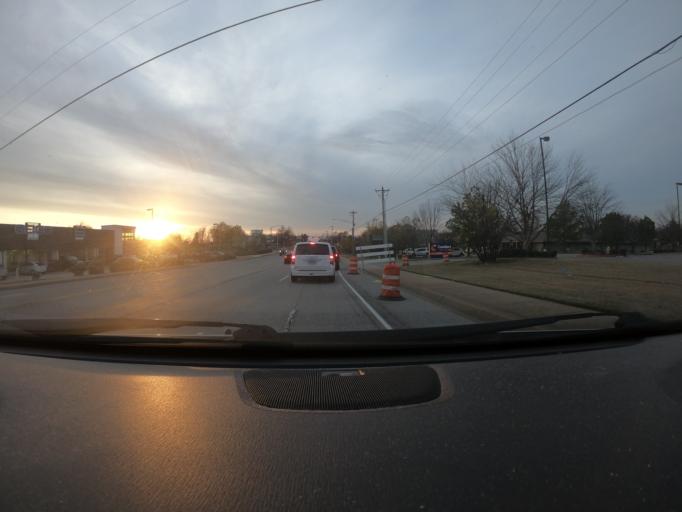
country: US
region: Arkansas
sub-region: Benton County
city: Bentonville
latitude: 36.3352
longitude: -94.1889
